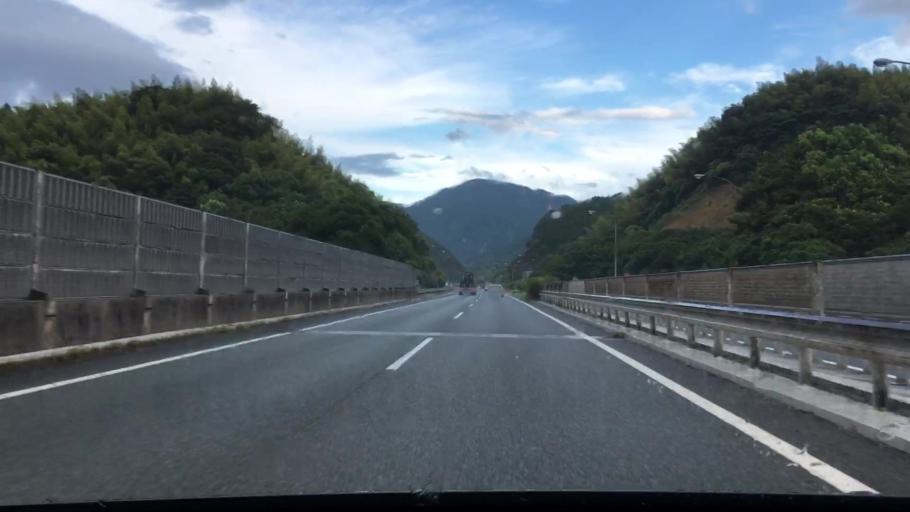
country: JP
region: Fukuoka
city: Kitakyushu
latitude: 33.8040
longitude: 130.8523
